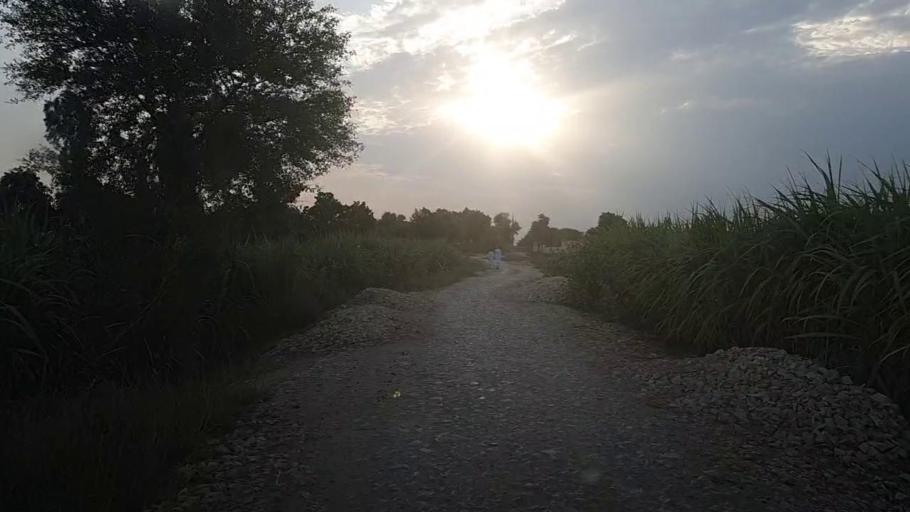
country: PK
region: Sindh
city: Ubauro
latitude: 28.3536
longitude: 69.7769
